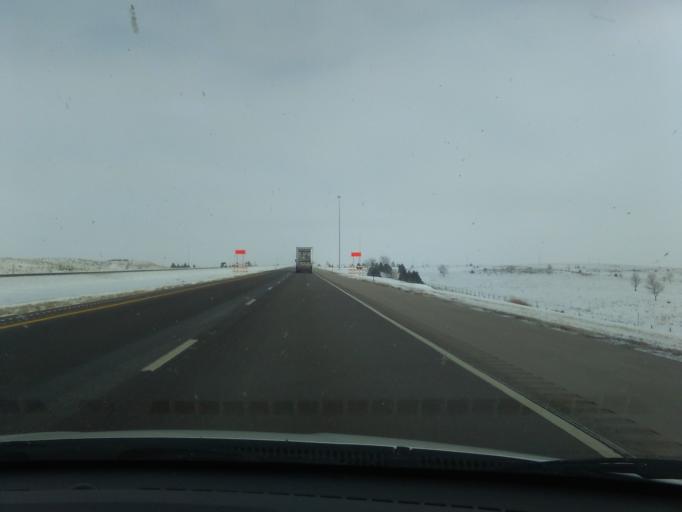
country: US
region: Nebraska
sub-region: Kimball County
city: Kimball
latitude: 41.2193
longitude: -103.6354
